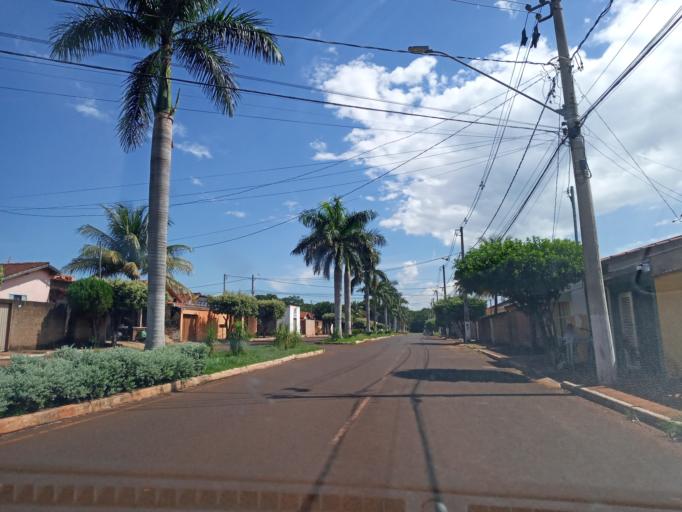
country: BR
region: Goias
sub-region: Itumbiara
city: Itumbiara
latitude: -18.4381
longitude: -49.1839
